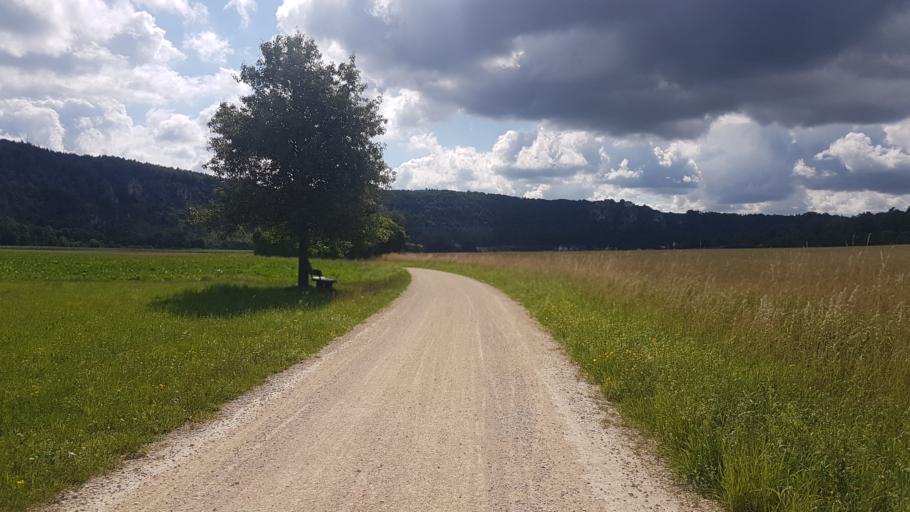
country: DE
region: Bavaria
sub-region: Upper Bavaria
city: Walting
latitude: 48.9349
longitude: 11.3607
